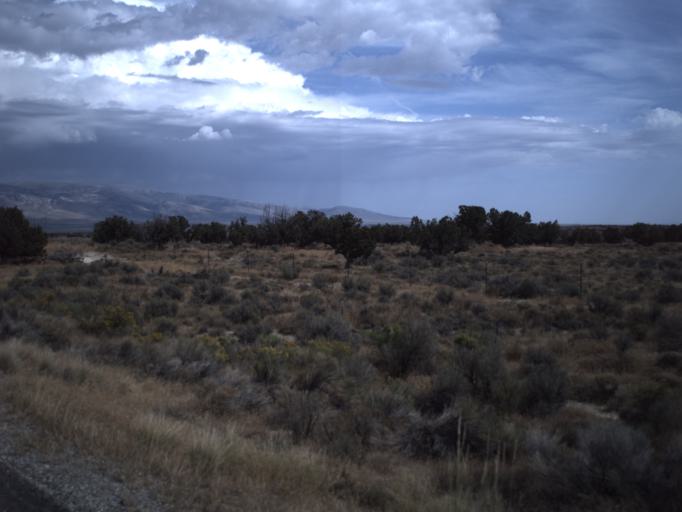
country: US
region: Idaho
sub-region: Cassia County
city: Burley
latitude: 41.7198
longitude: -113.5268
